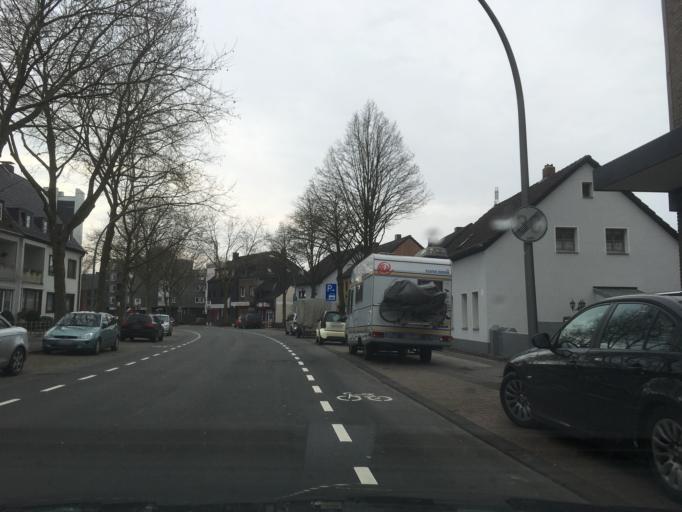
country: DE
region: North Rhine-Westphalia
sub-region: Regierungsbezirk Munster
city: Gladbeck
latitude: 51.5800
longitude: 7.0008
